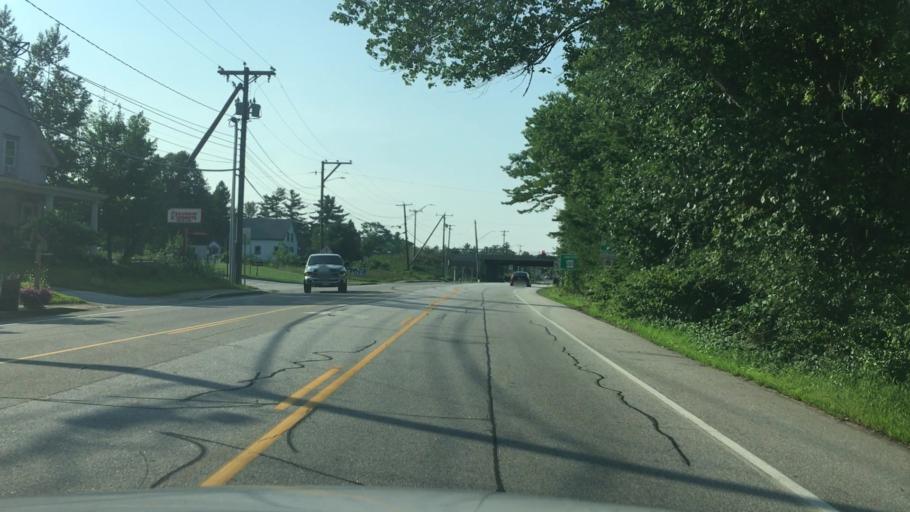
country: US
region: New Hampshire
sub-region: Rockingham County
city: Auburn
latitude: 43.0050
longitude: -71.3934
